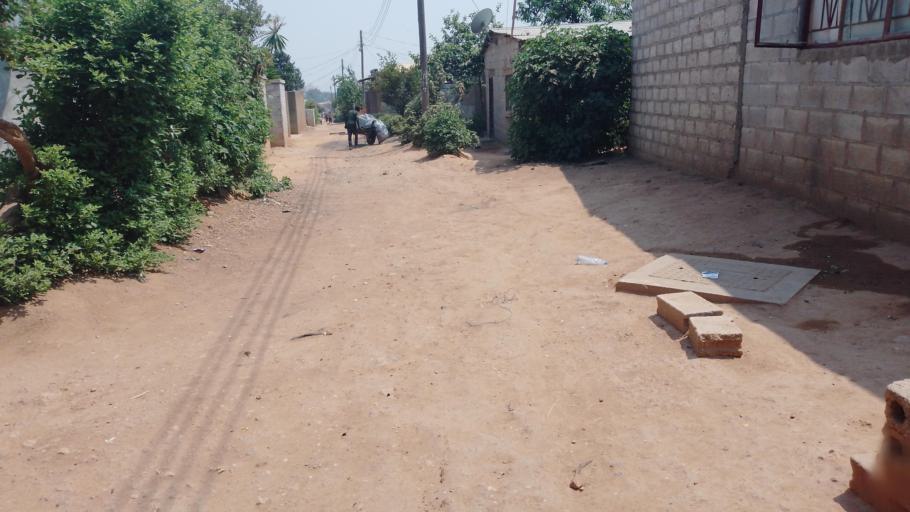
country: ZM
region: Lusaka
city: Lusaka
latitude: -15.3959
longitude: 28.3759
